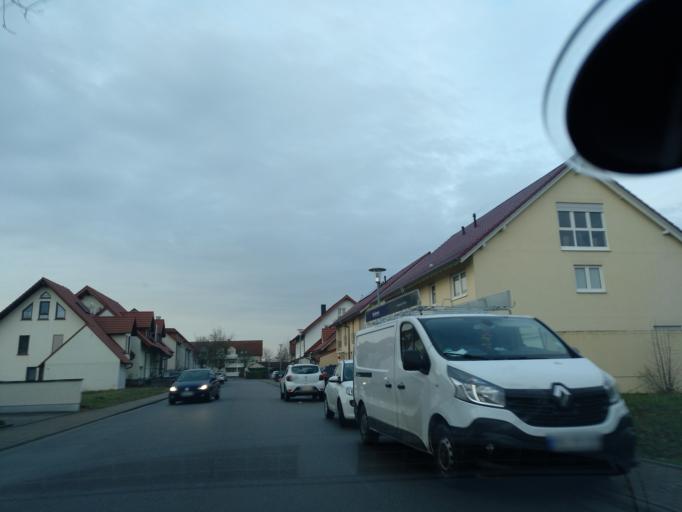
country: DE
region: Baden-Wuerttemberg
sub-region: Karlsruhe Region
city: Reilingen
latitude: 49.2986
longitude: 8.5650
